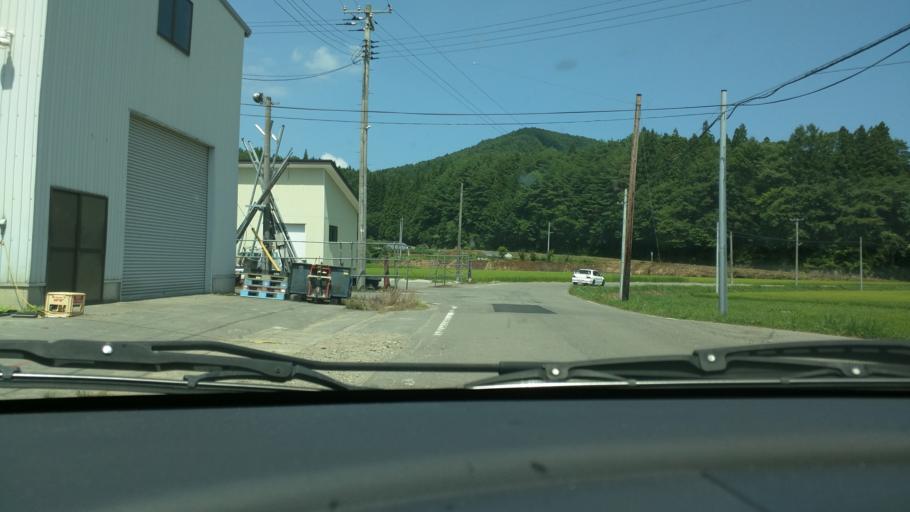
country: JP
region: Fukushima
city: Inawashiro
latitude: 37.3916
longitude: 140.0664
